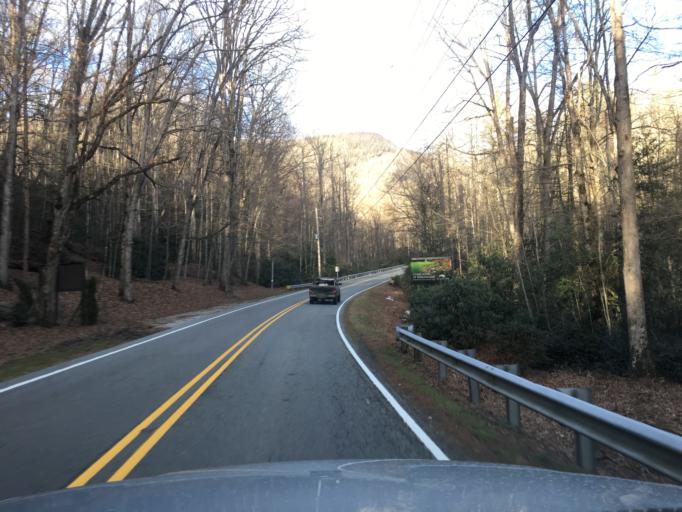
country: US
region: North Carolina
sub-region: Jackson County
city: Cullowhee
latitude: 35.1126
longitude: -82.9889
